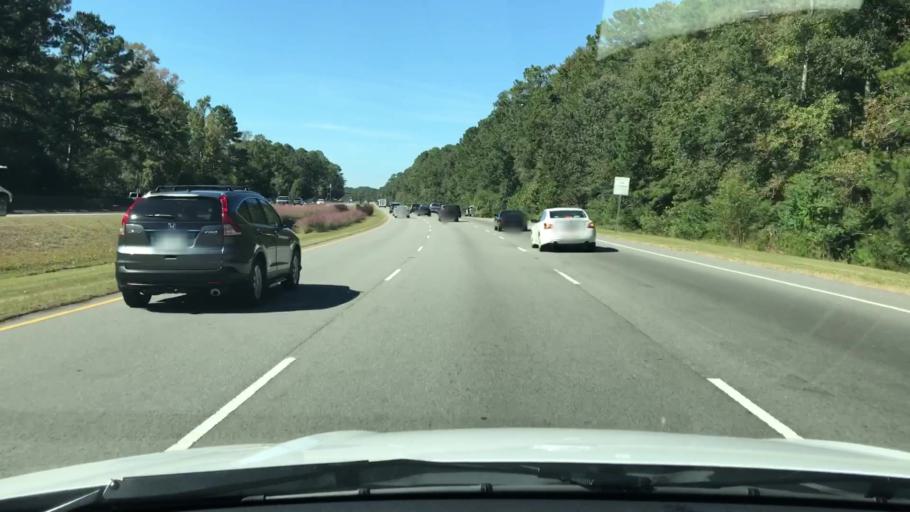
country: US
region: South Carolina
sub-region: Beaufort County
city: Bluffton
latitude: 32.2809
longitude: -80.8753
